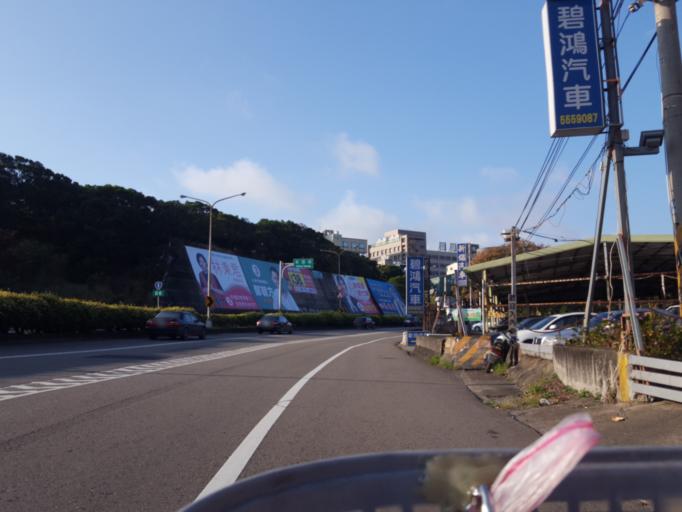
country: TW
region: Taiwan
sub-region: Hsinchu
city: Zhubei
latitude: 24.8599
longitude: 120.9918
